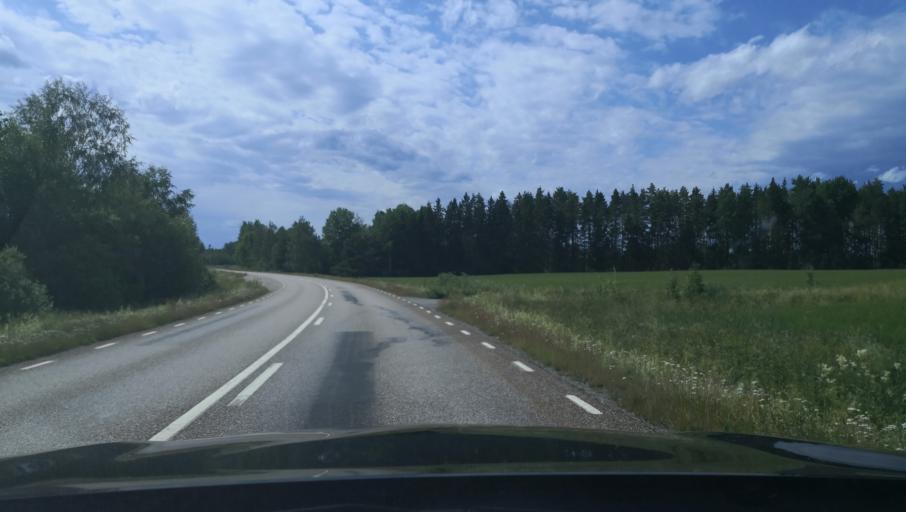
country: SE
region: Dalarna
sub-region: Avesta Kommun
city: Avesta
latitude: 59.9643
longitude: 16.2066
